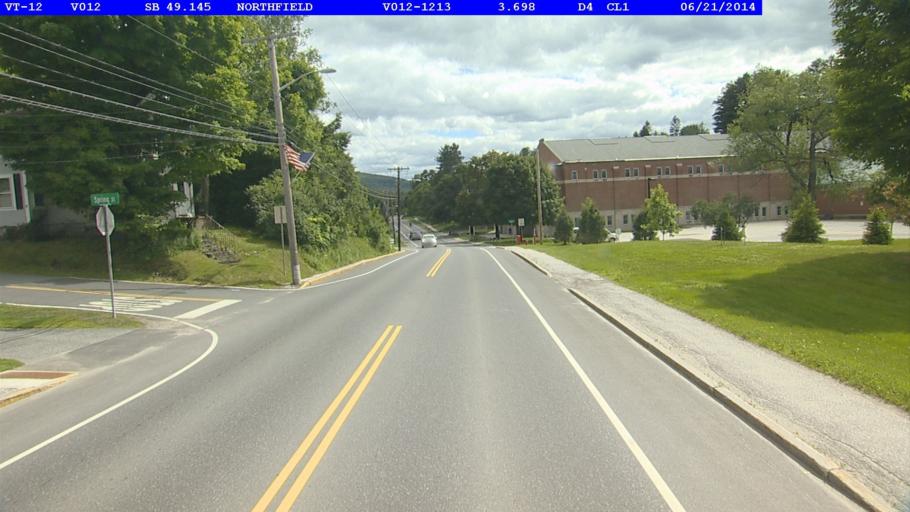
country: US
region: Vermont
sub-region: Washington County
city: Northfield
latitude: 44.1419
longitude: -72.6573
